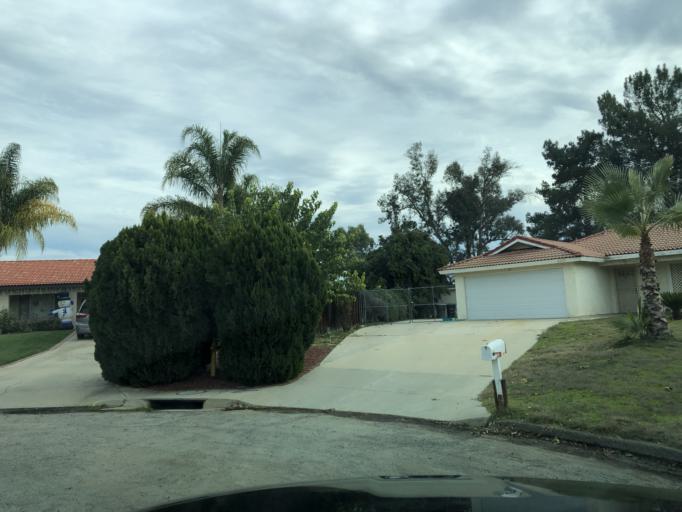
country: US
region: California
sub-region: Riverside County
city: Wildomar
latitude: 33.6091
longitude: -117.2703
